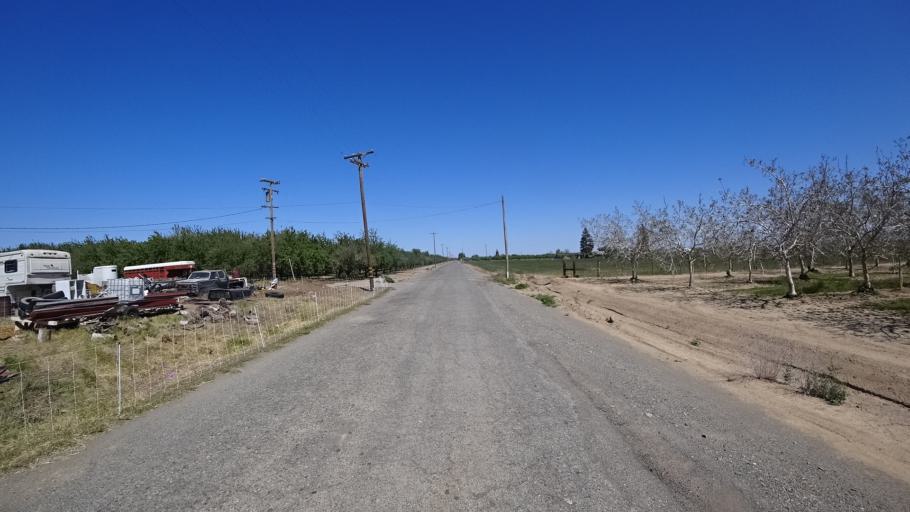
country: US
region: California
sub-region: Glenn County
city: Orland
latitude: 39.7032
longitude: -122.1547
